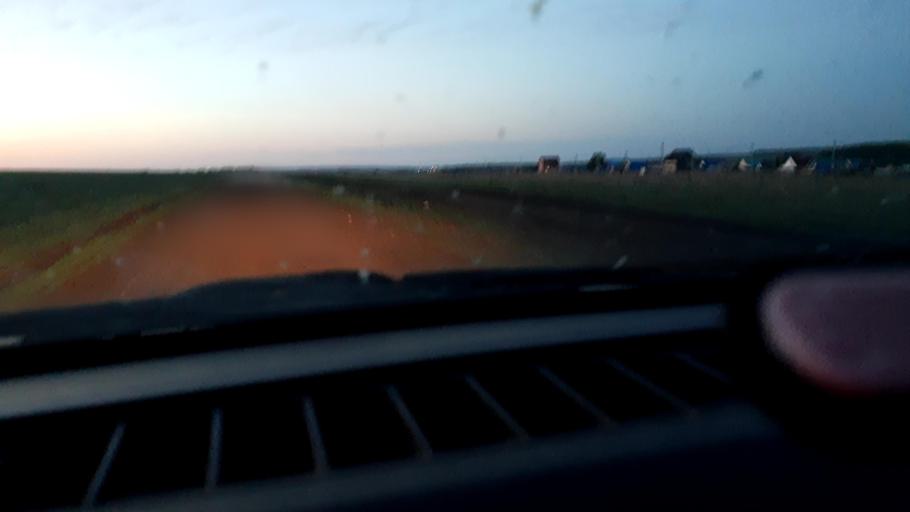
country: RU
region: Bashkortostan
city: Asanovo
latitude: 54.8565
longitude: 55.5856
